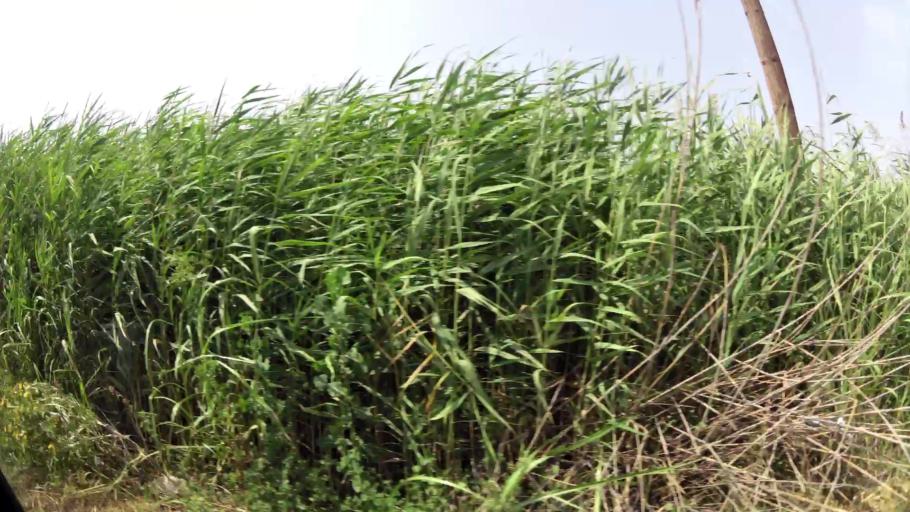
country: GR
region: Central Macedonia
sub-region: Nomos Thessalonikis
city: Menemeni
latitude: 40.6611
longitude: 22.8946
